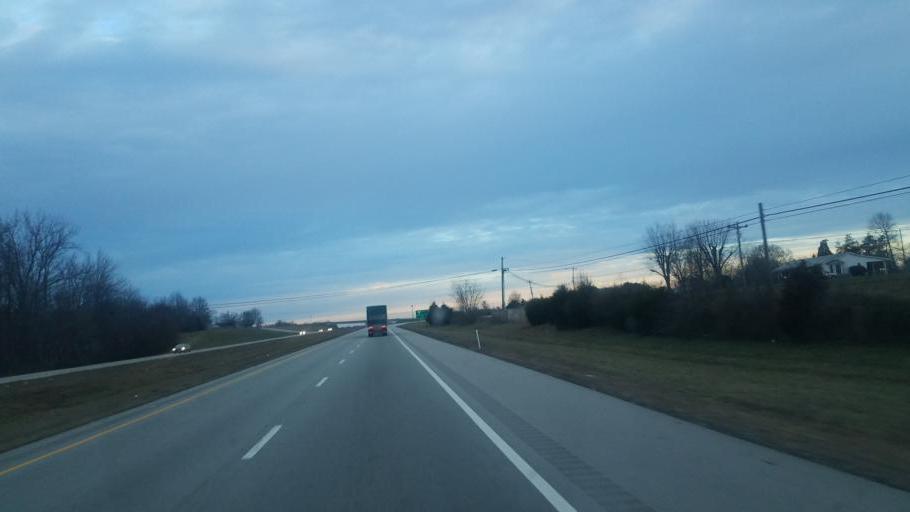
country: US
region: Tennessee
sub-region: Putnam County
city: Cookeville
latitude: 36.0484
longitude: -85.5077
